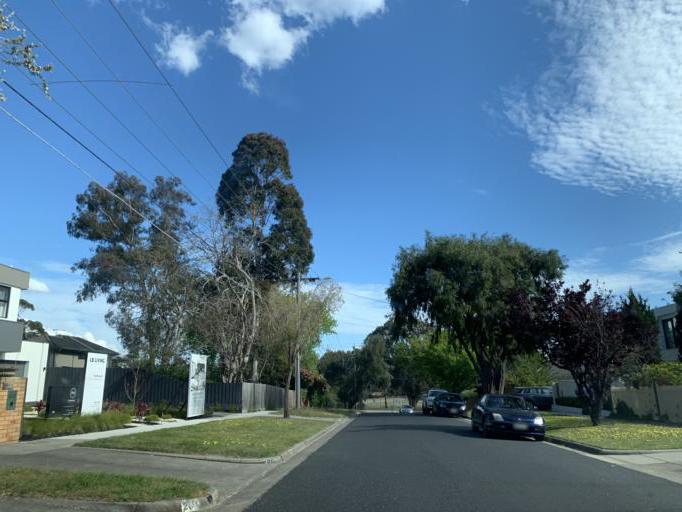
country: AU
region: Victoria
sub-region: Bayside
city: Black Rock
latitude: -37.9621
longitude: 145.0260
